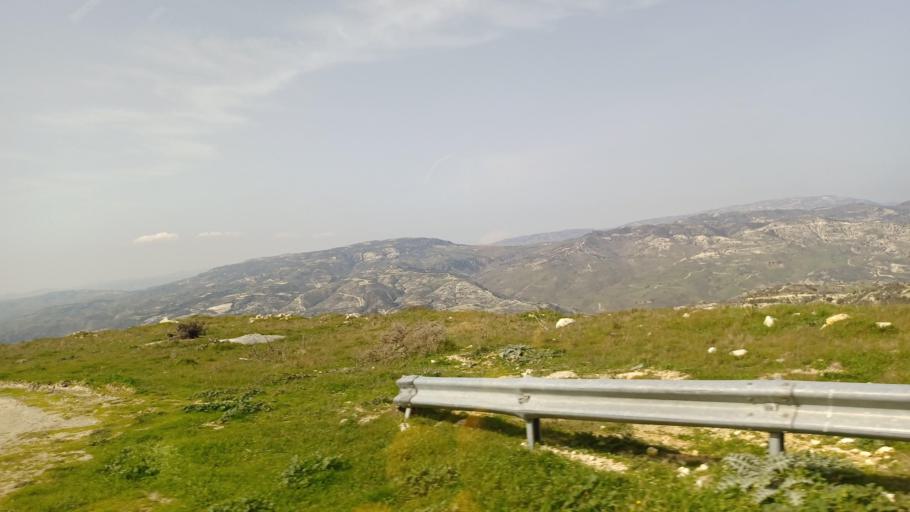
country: CY
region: Limassol
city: Pachna
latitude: 34.7939
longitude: 32.7379
